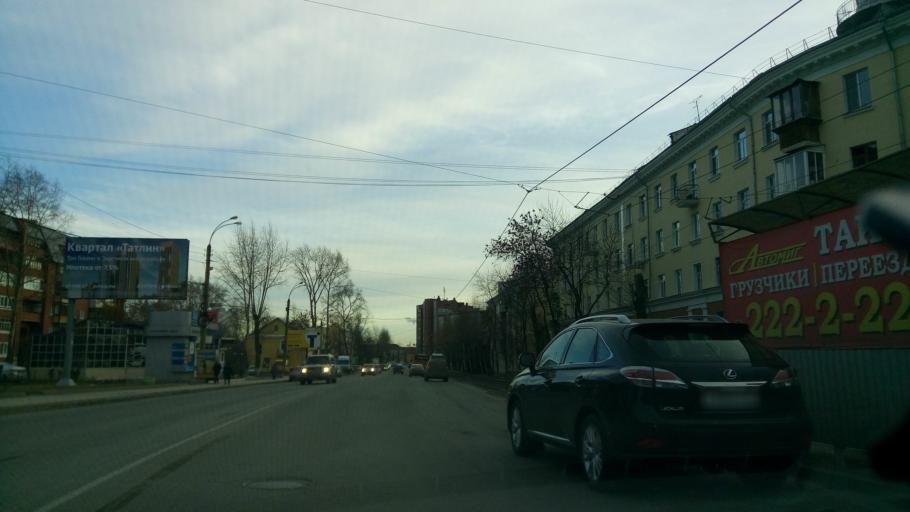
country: RU
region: Sverdlovsk
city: Shuvakish
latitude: 56.8738
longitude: 60.5184
